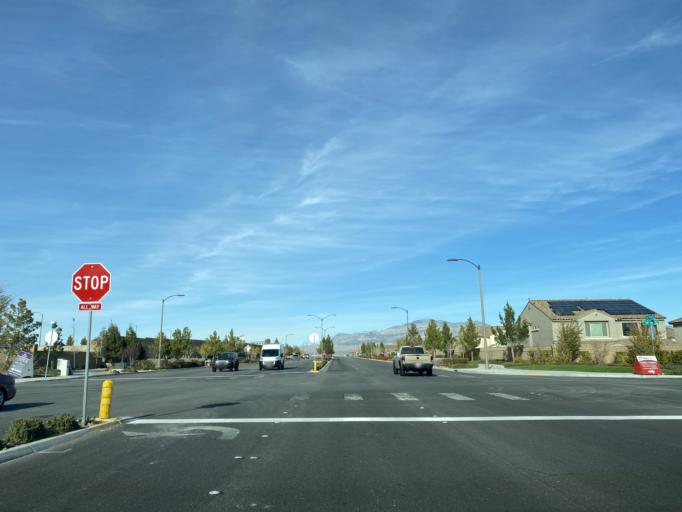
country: US
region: Nevada
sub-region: Clark County
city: Summerlin South
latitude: 36.3102
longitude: -115.3149
